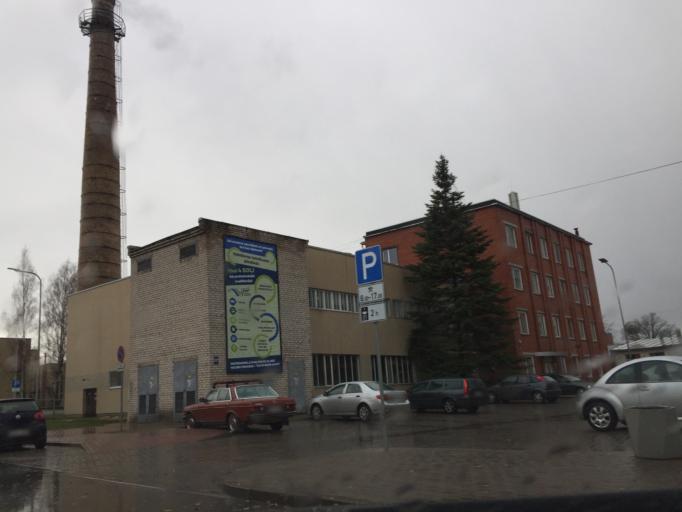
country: LV
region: Valmieras Rajons
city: Valmiera
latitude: 57.5379
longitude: 25.4161
